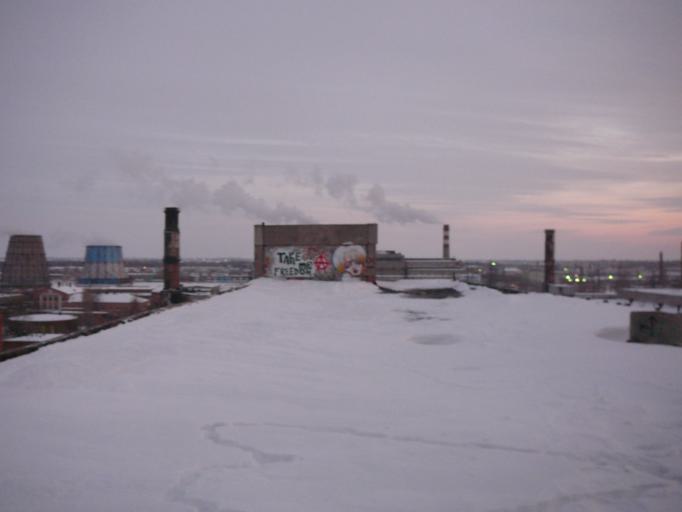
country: RU
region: Saratov
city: Engel's
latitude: 51.4670
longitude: 46.1503
